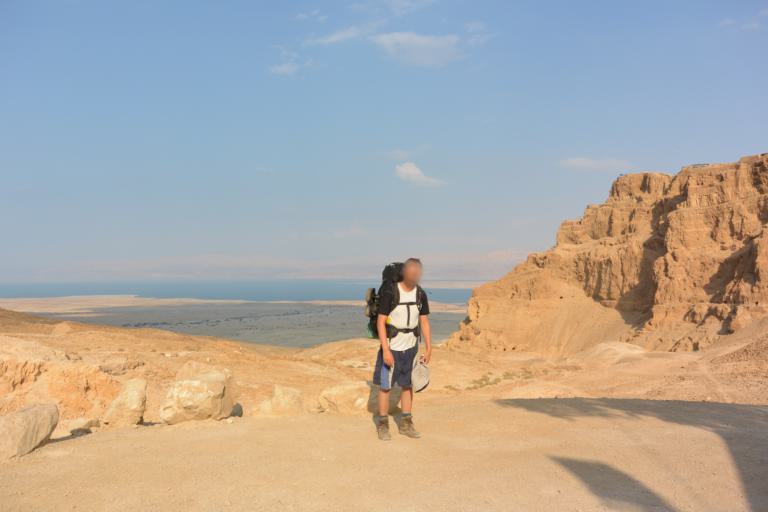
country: IL
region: Southern District
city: `En Boqeq
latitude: 31.3179
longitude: 35.3488
